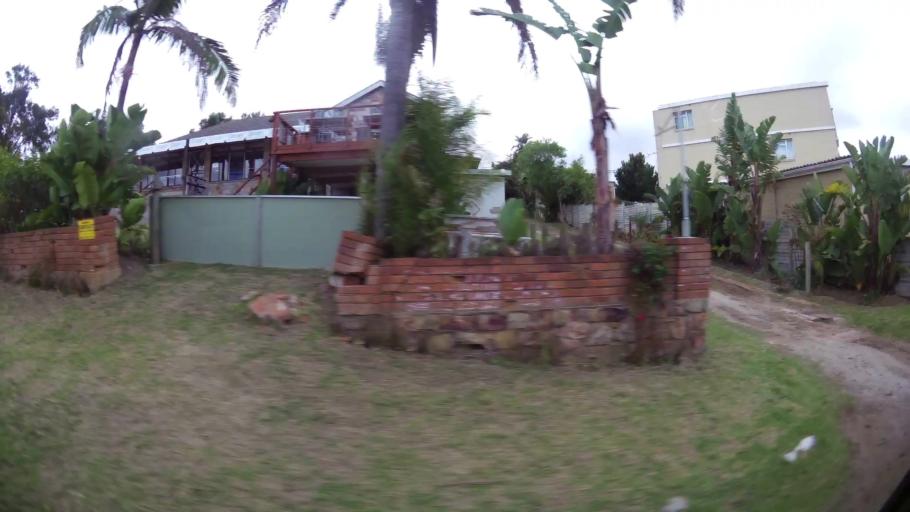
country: ZA
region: Western Cape
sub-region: Eden District Municipality
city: Plettenberg Bay
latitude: -34.0561
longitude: 23.3732
